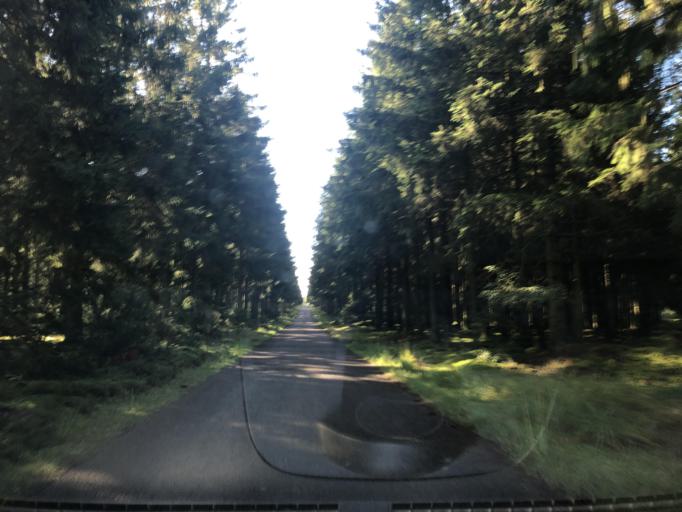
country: DK
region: Central Jutland
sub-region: Holstebro Kommune
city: Holstebro
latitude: 56.3173
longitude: 8.5075
